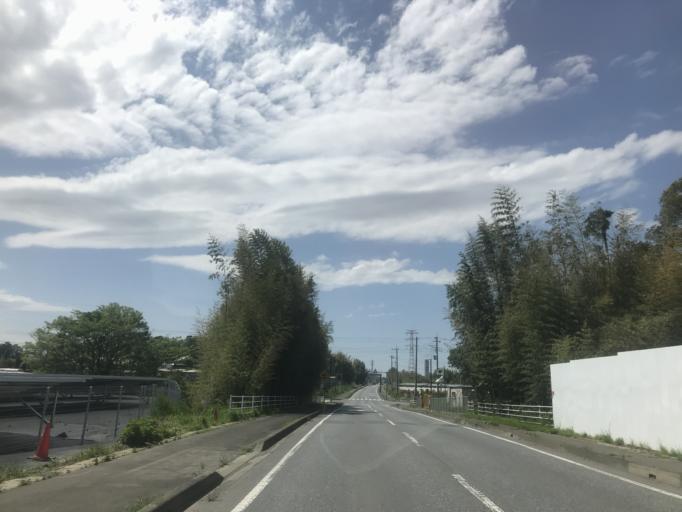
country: JP
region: Chiba
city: Noda
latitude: 35.9660
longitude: 139.8985
